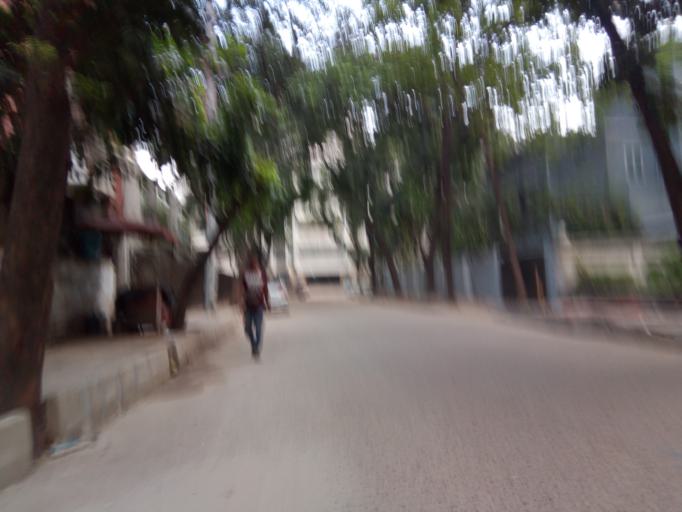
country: BD
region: Dhaka
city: Paltan
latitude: 23.7796
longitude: 90.4130
